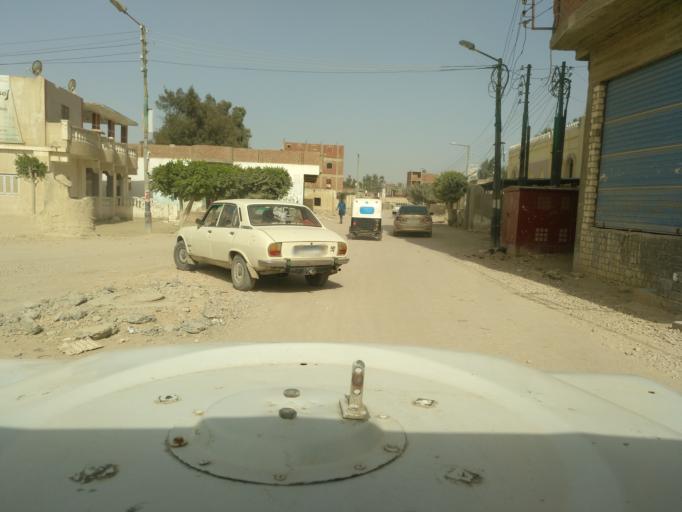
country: EG
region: Al Buhayrah
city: Beheira
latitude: 30.3722
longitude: 30.3531
